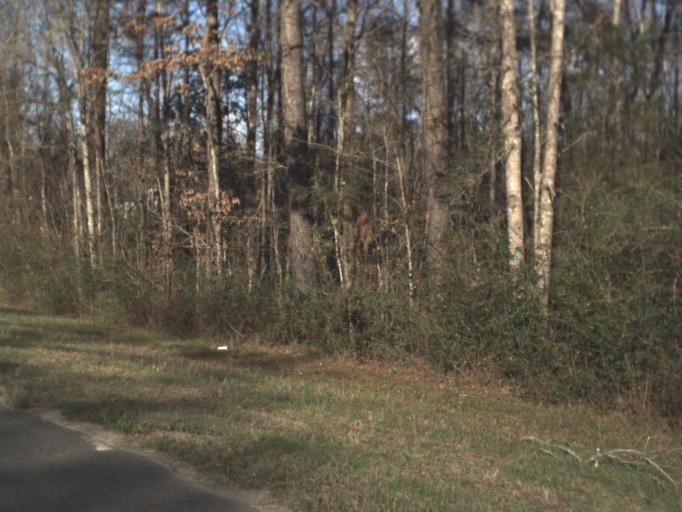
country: US
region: Florida
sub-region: Jackson County
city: Marianna
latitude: 30.7028
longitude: -85.2318
